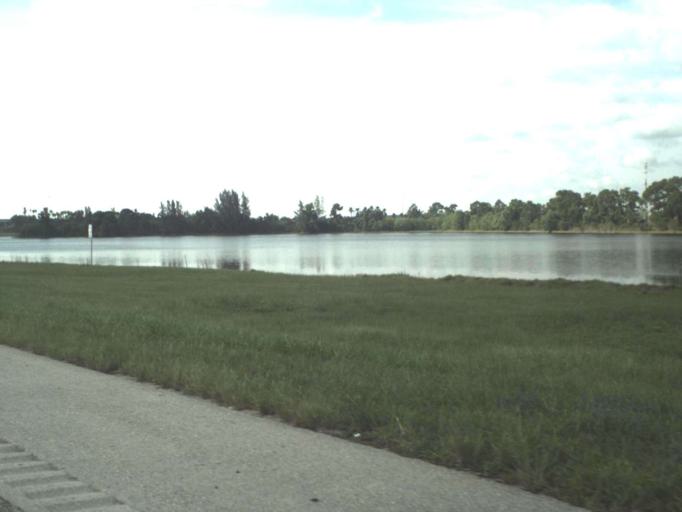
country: US
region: Florida
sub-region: Palm Beach County
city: Limestone Creek
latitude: 26.9449
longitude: -80.1559
